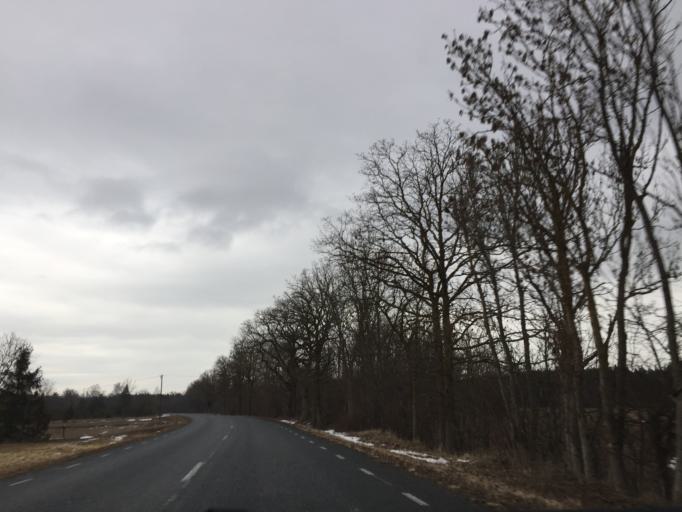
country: EE
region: Saare
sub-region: Orissaare vald
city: Orissaare
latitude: 58.5564
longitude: 22.7747
